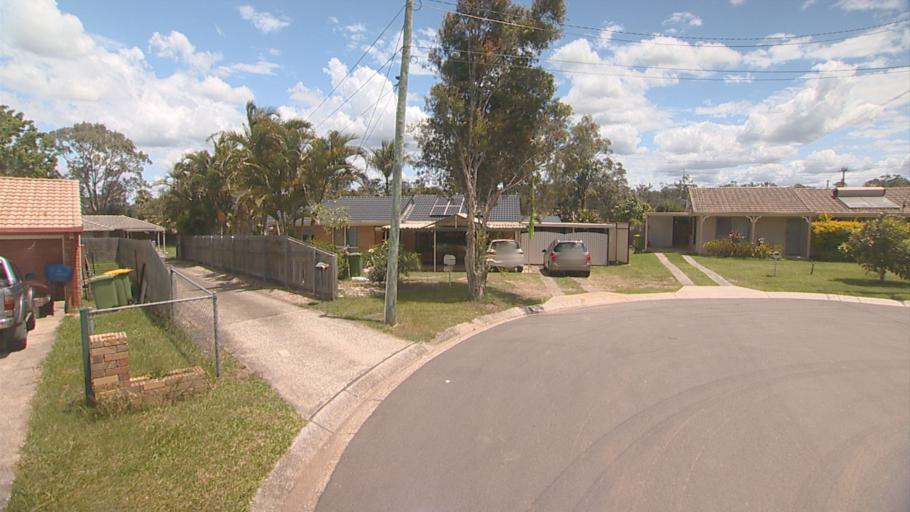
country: AU
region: Queensland
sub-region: Logan
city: Logan City
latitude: -27.6615
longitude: 153.0993
